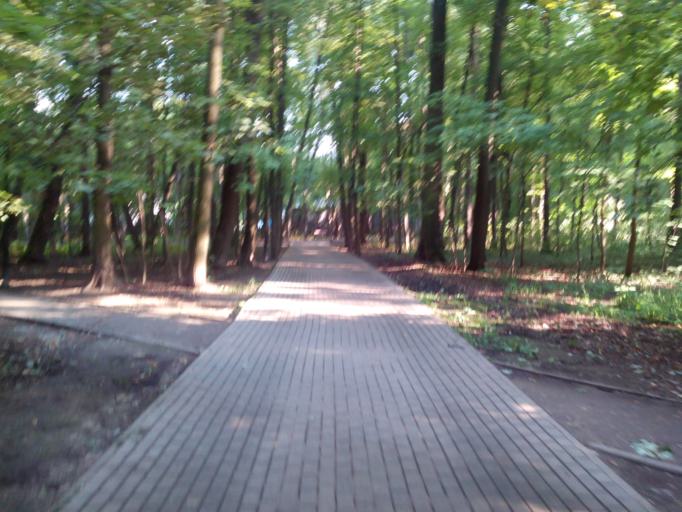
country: RU
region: Moskovskaya
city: Fili
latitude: 55.7472
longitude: 37.4863
